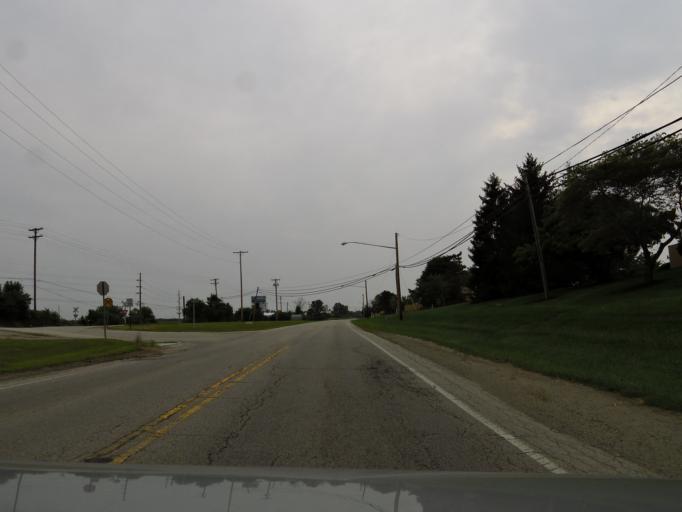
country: US
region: Ohio
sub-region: Clinton County
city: Wilmington
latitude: 39.4303
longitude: -83.8321
